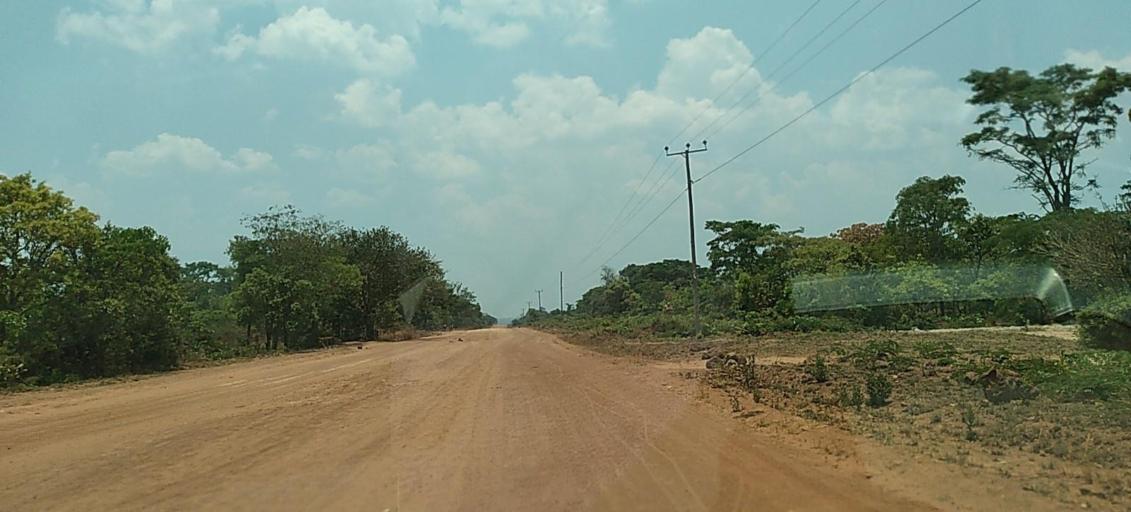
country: ZM
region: Copperbelt
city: Chingola
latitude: -12.8973
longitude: 27.5756
